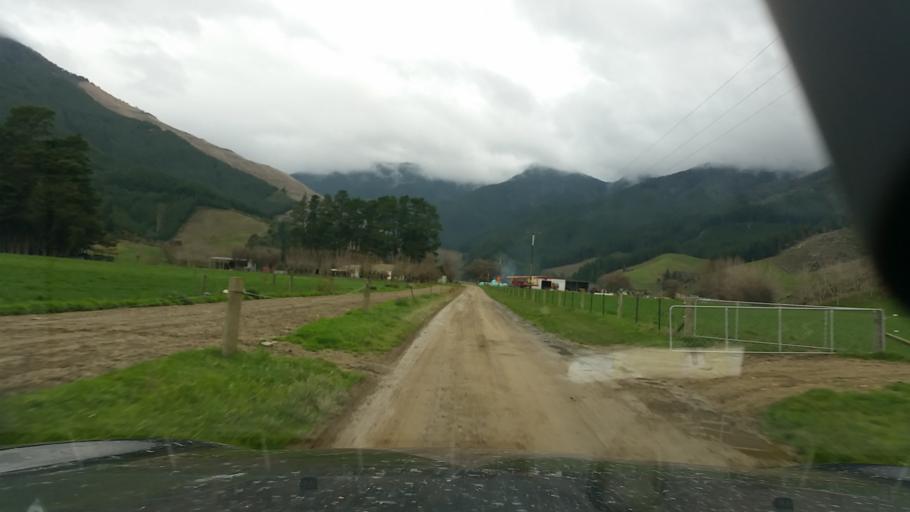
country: NZ
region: Marlborough
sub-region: Marlborough District
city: Picton
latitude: -41.3007
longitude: 173.8549
